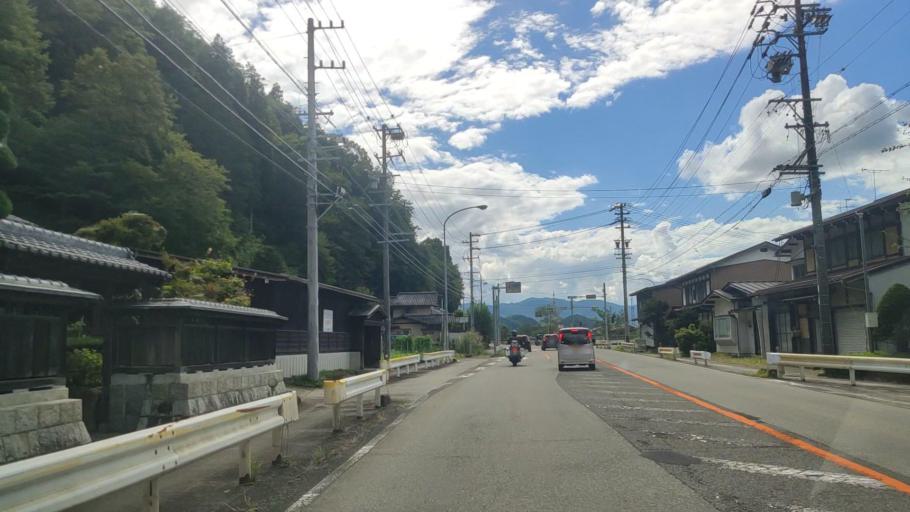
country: JP
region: Gifu
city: Takayama
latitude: 36.1805
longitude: 137.2506
